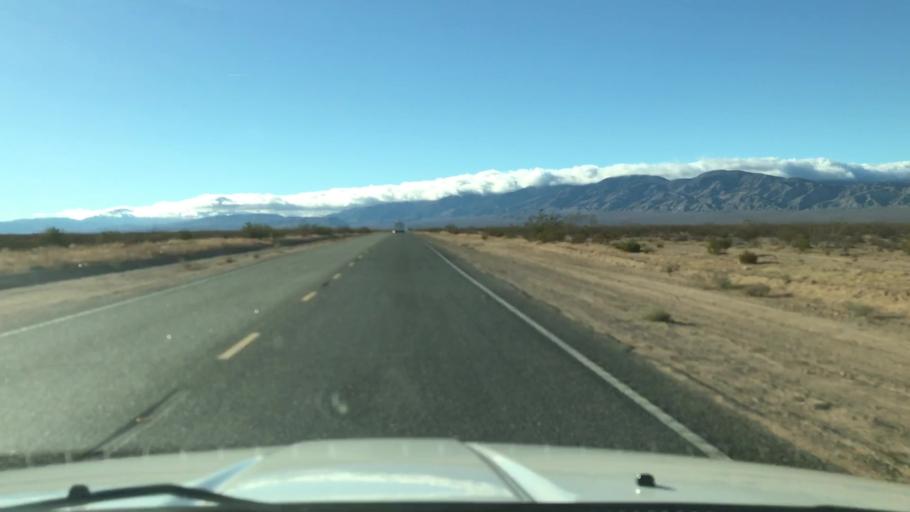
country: US
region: California
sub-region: Kern County
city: California City
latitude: 35.1255
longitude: -118.0471
